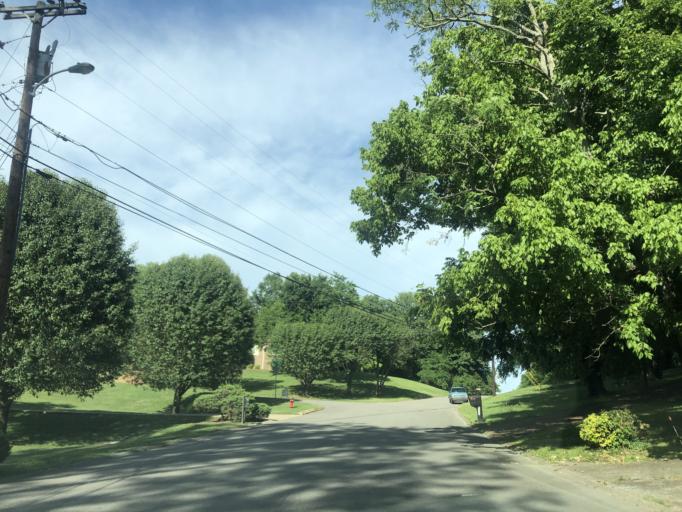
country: US
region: Tennessee
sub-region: Davidson County
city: Nashville
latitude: 36.2224
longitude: -86.8347
